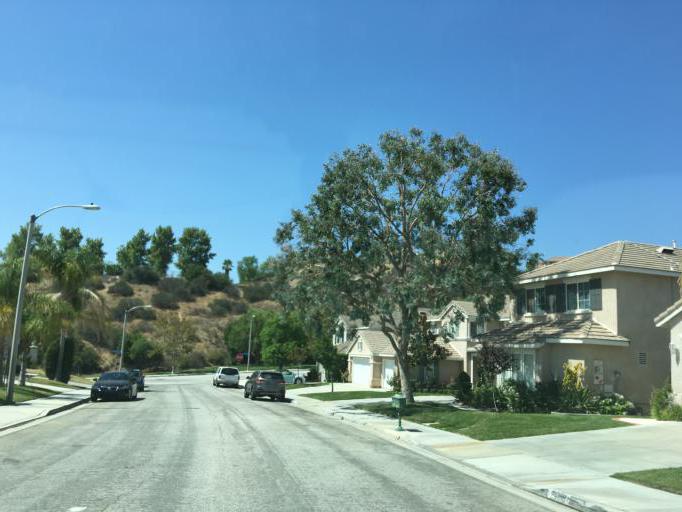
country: US
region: California
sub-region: Los Angeles County
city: Santa Clarita
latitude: 34.3945
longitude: -118.5922
